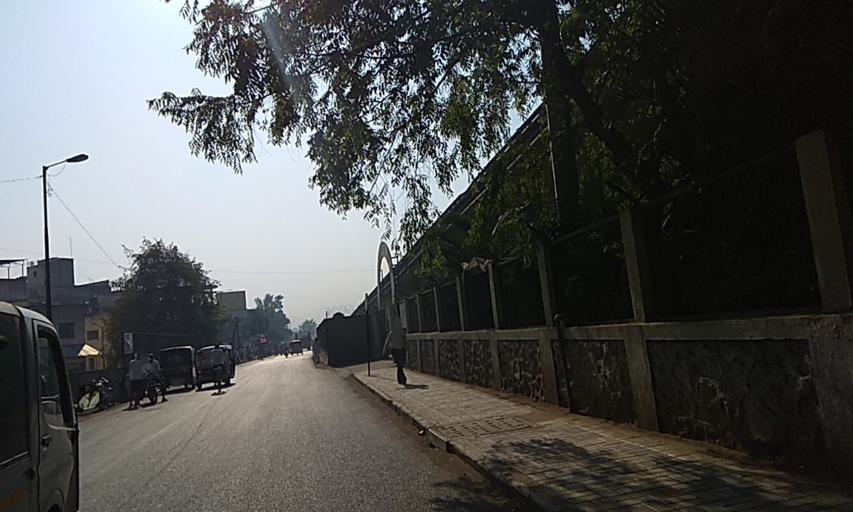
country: IN
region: Maharashtra
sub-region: Pune Division
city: Kharakvasla
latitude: 18.4797
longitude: 73.8051
